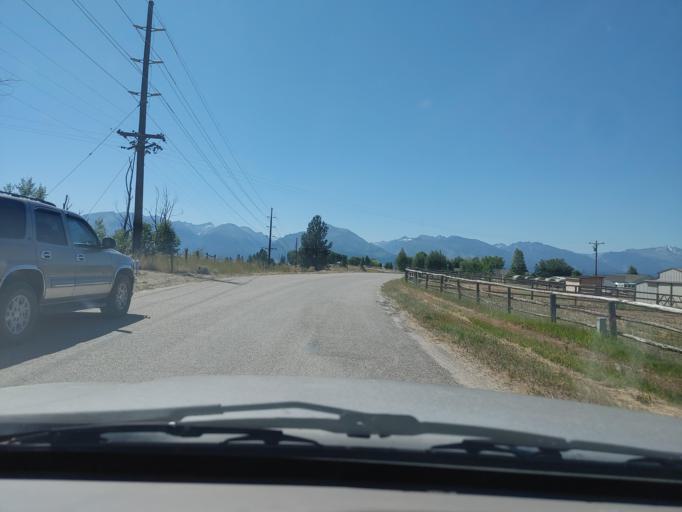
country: US
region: Montana
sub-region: Ravalli County
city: Hamilton
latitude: 46.2768
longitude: -114.0388
